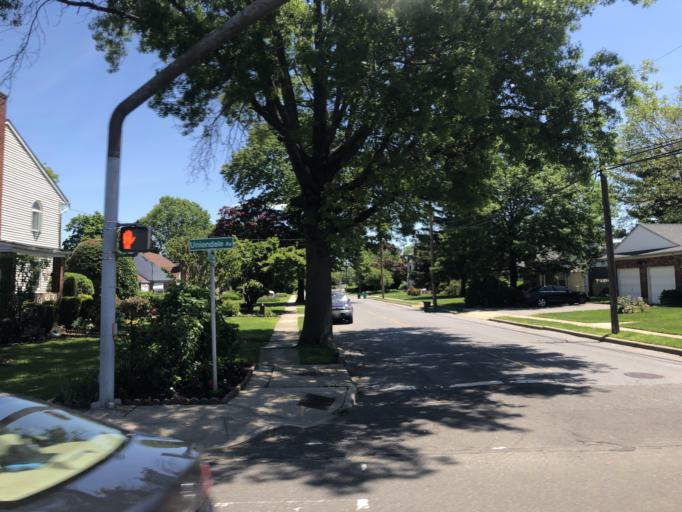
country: US
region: New York
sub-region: Nassau County
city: Uniondale
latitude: 40.6962
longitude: -73.5947
